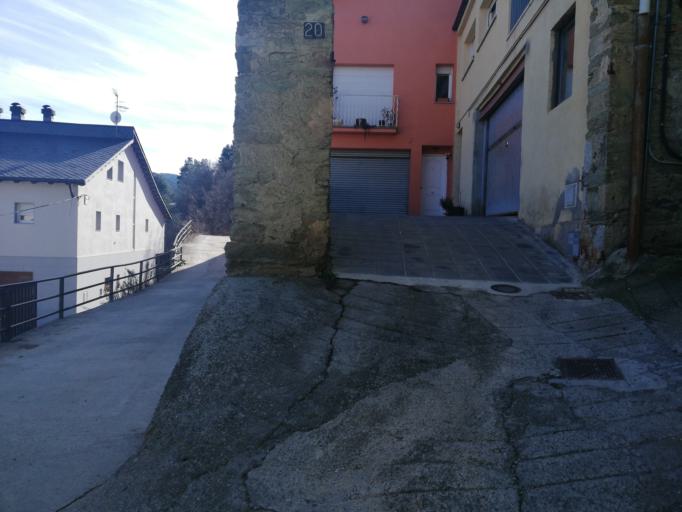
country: ES
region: Catalonia
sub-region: Provincia de Lleida
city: la Seu d'Urgell
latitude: 42.3537
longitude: 1.4433
